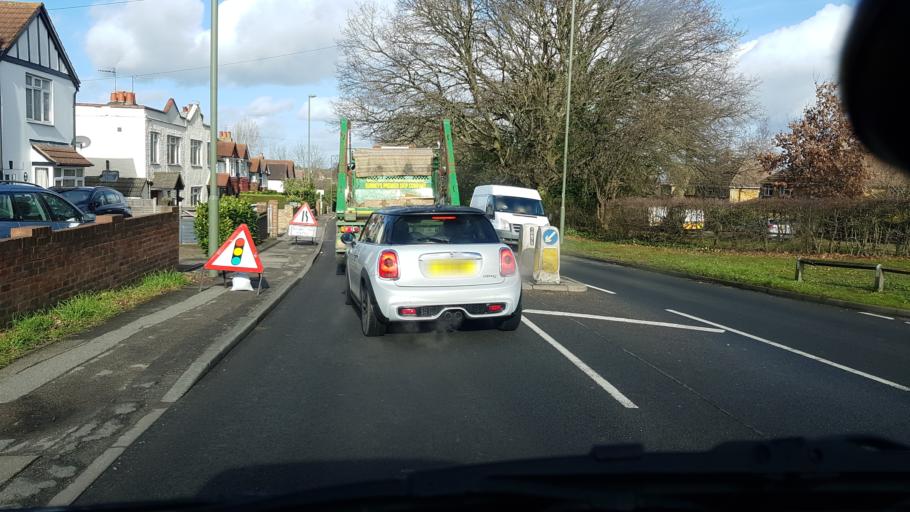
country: GB
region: England
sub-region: Surrey
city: Guildford
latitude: 51.2599
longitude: -0.5952
